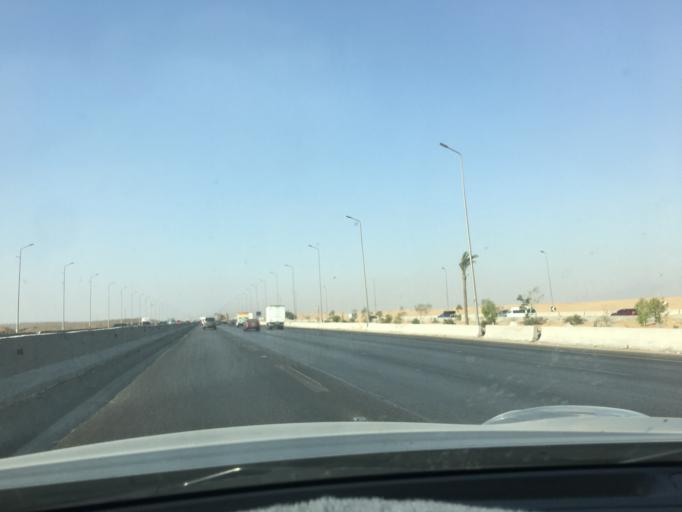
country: EG
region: Muhafazat al Qalyubiyah
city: Al Khankah
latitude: 30.1042
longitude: 31.4503
